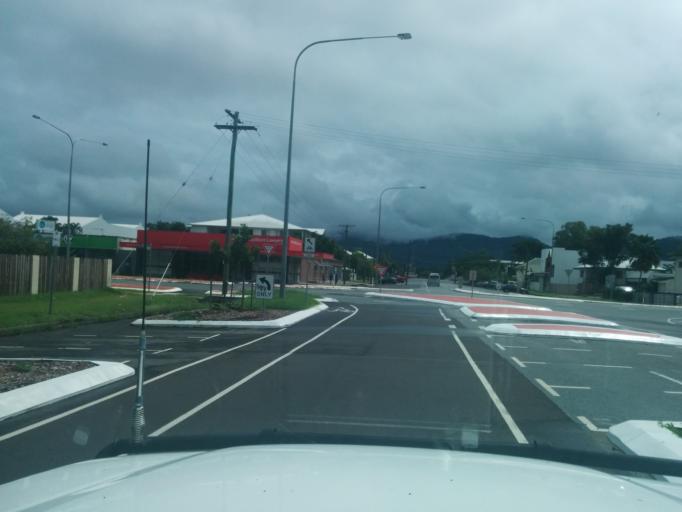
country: AU
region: Queensland
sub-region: Cairns
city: Cairns
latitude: -16.9192
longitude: 145.7687
